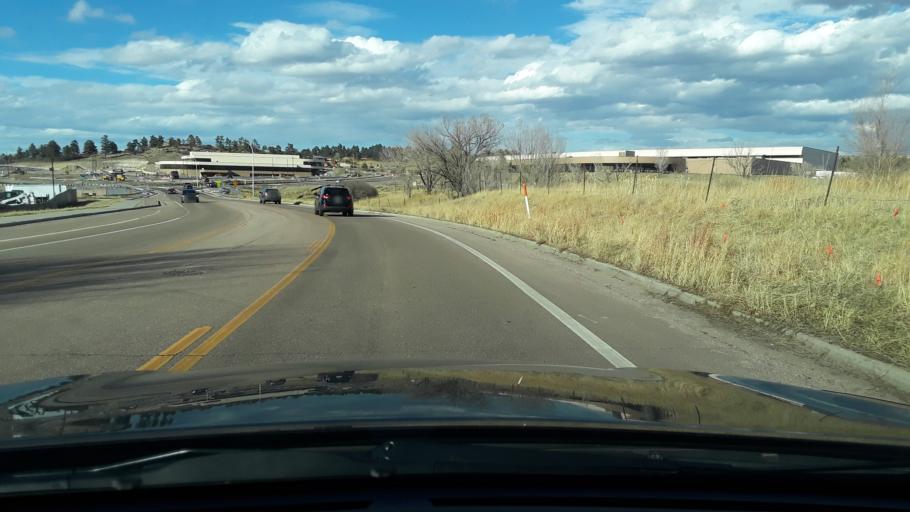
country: US
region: Colorado
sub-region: El Paso County
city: Air Force Academy
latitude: 38.9267
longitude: -104.8100
